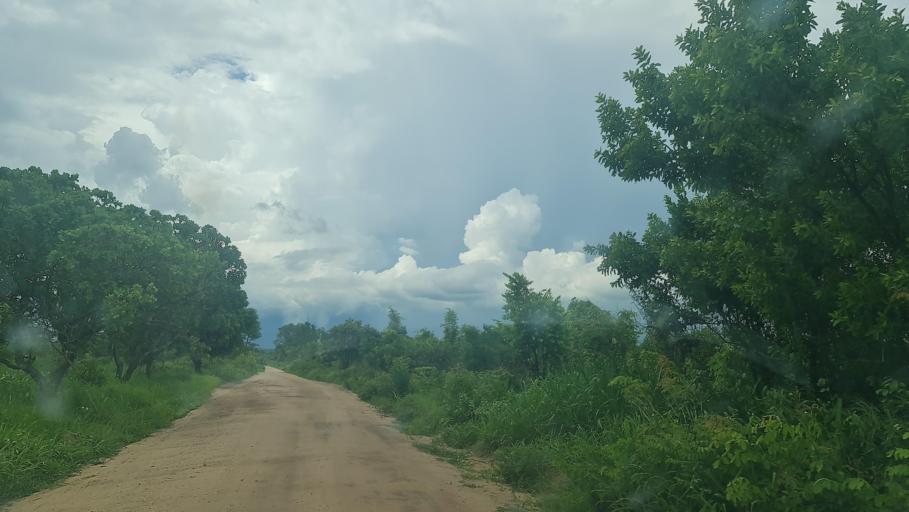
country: MW
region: Southern Region
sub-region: Nsanje District
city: Nsanje
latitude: -17.5937
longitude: 35.6749
